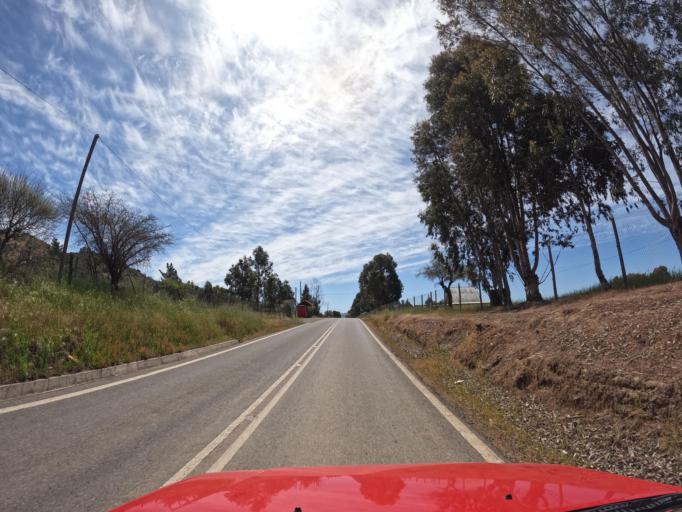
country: CL
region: Maule
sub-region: Provincia de Talca
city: Talca
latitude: -35.0520
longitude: -71.7492
